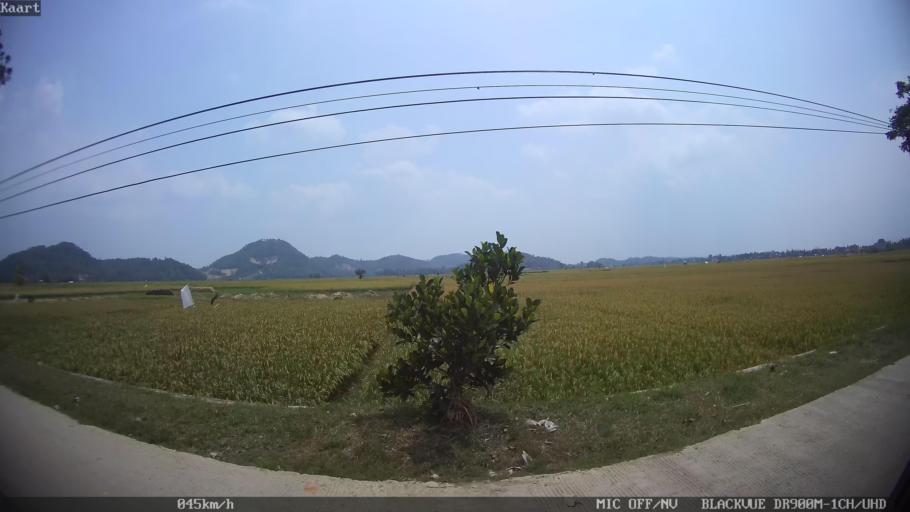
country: ID
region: Lampung
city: Pringsewu
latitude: -5.3675
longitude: 105.0081
